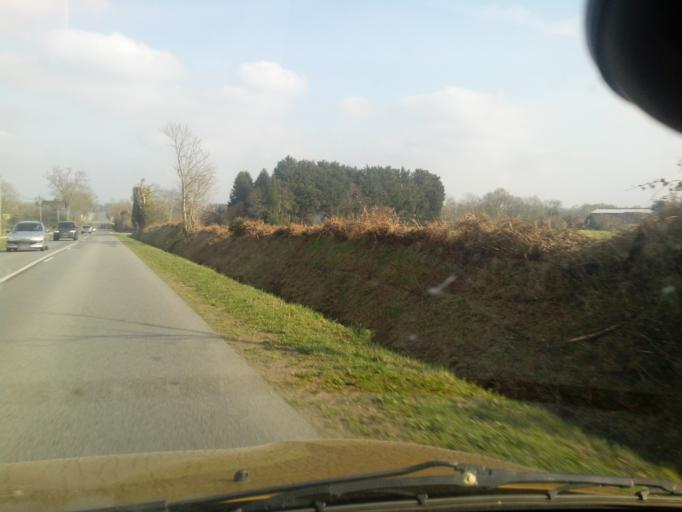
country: FR
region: Brittany
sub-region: Departement du Morbihan
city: La Vraie-Croix
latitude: 47.6954
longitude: -2.5024
